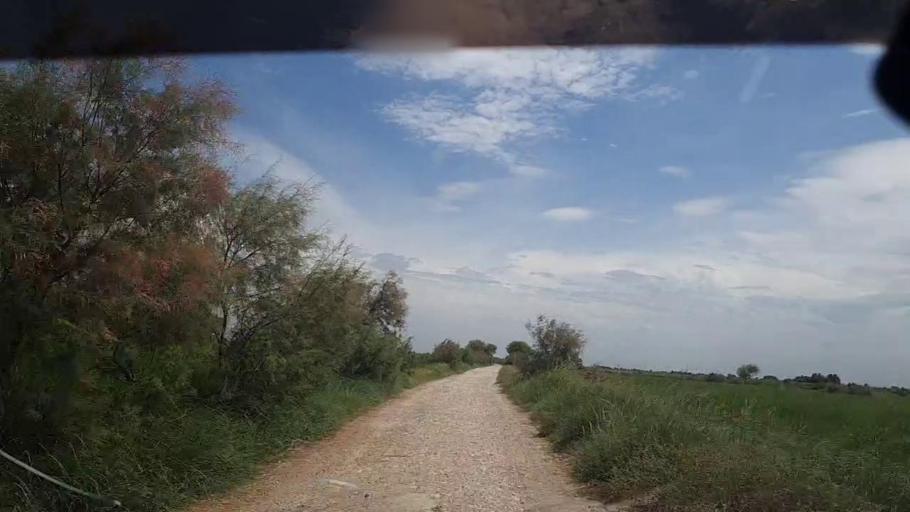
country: PK
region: Sindh
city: Ghauspur
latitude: 28.1465
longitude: 68.9771
